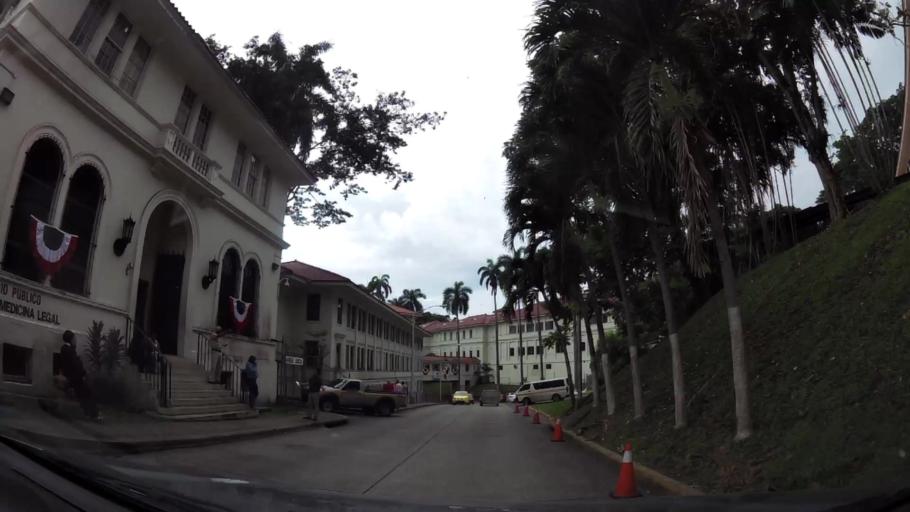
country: PA
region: Panama
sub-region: Distrito de Panama
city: Ancon
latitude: 8.9613
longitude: -79.5472
